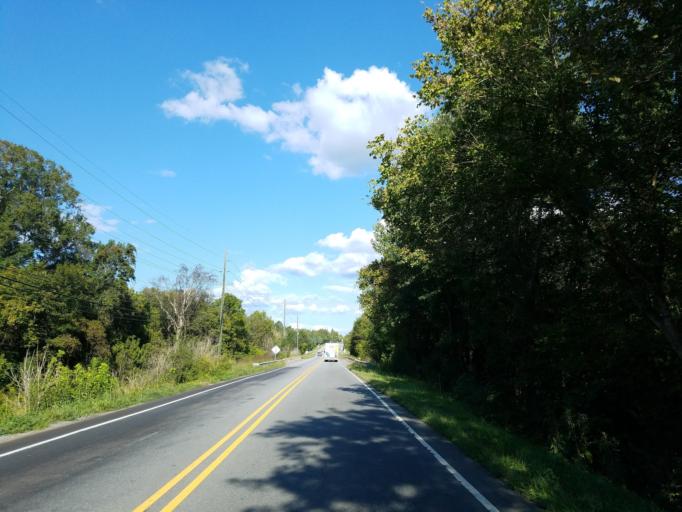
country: US
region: North Carolina
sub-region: Davidson County
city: Lexington
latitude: 35.7993
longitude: -80.3016
